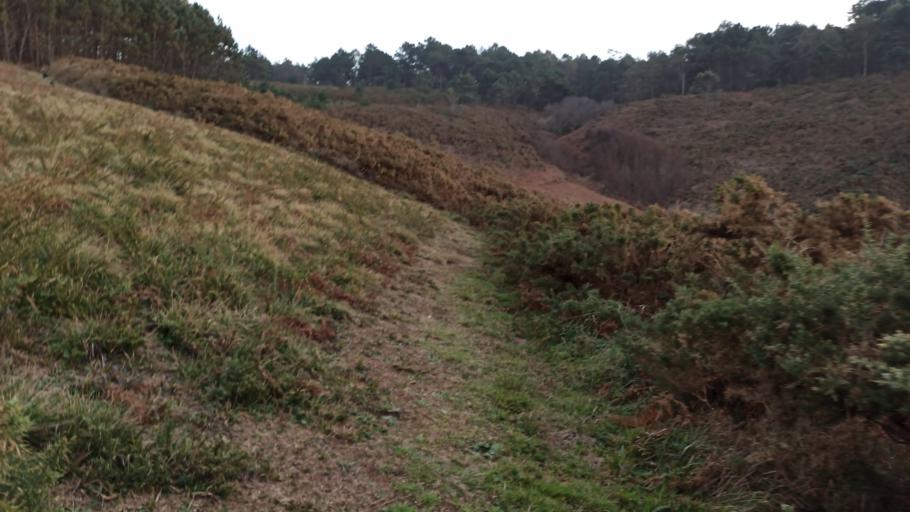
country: ES
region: Galicia
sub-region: Provincia da Coruna
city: A Coruna
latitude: 43.3987
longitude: -8.3363
